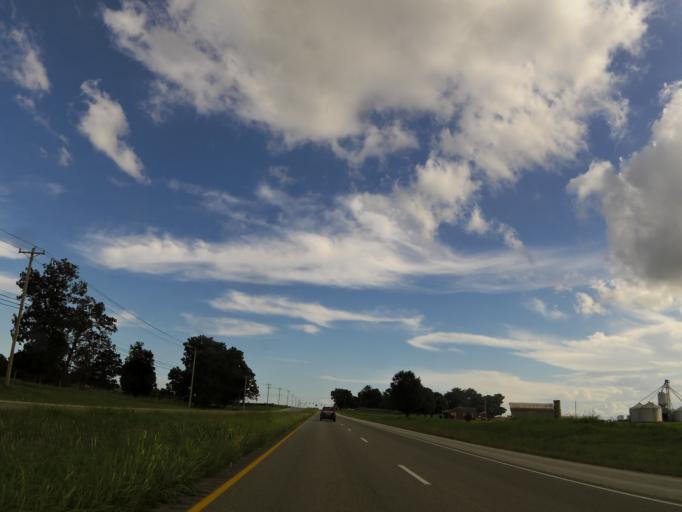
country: US
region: Kentucky
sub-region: Christian County
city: Oak Grove
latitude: 36.7391
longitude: -87.4655
